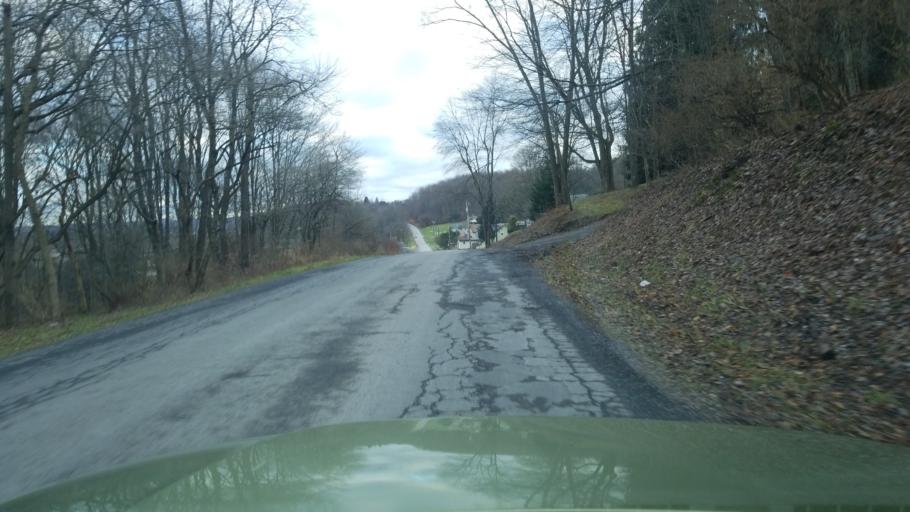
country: US
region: Pennsylvania
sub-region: Jefferson County
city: Falls Creek
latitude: 41.1343
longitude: -78.7864
